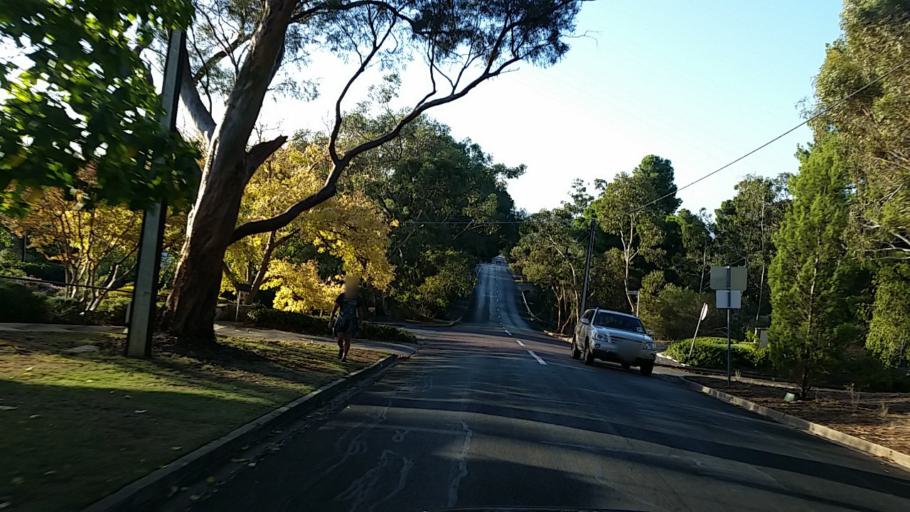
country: AU
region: South Australia
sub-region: Mitcham
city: Mitcham
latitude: -34.9818
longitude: 138.6277
